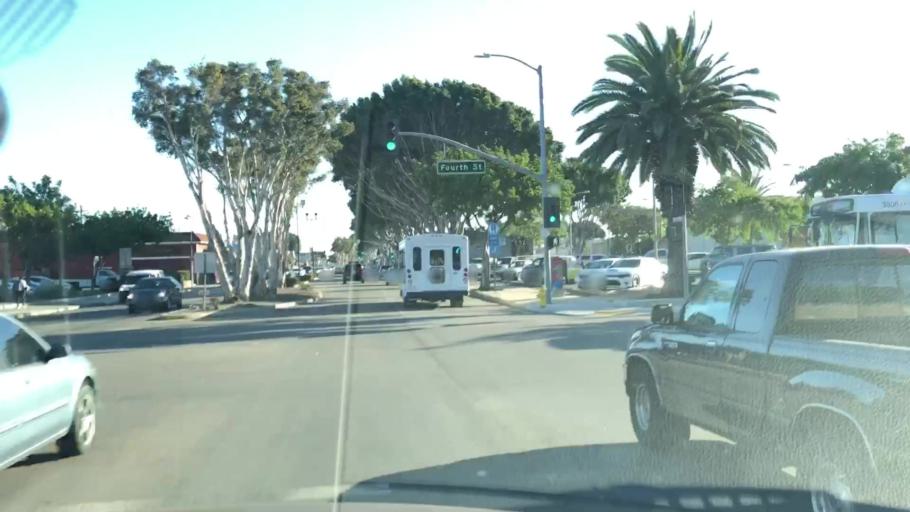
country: US
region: California
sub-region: Ventura County
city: Oxnard
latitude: 34.1991
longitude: -119.1774
